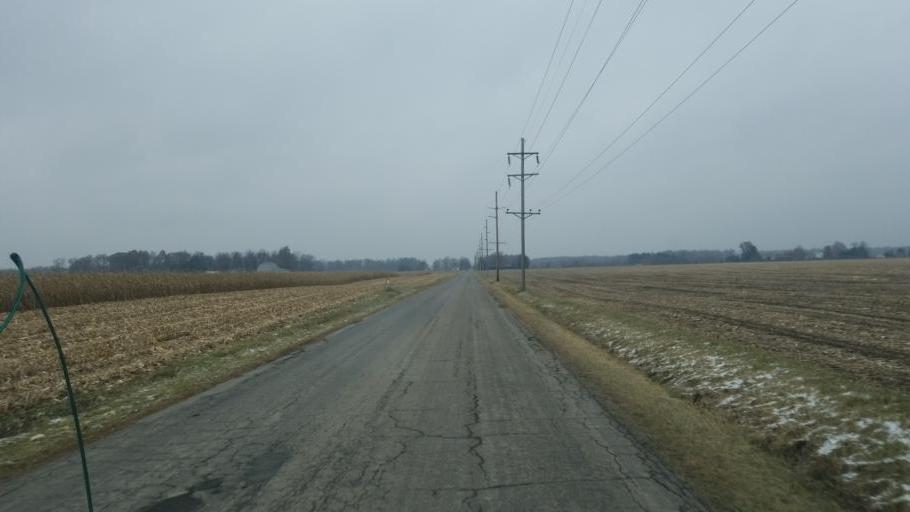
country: US
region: Ohio
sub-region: Richland County
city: Shelby
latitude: 40.9242
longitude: -82.6860
